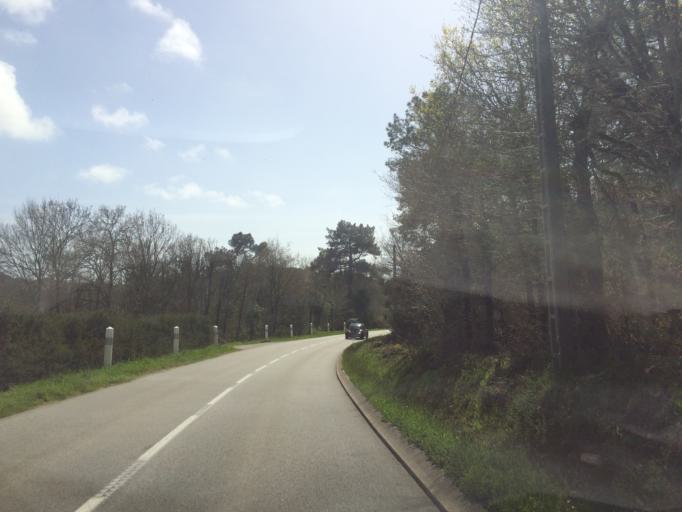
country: FR
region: Brittany
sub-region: Departement du Morbihan
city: Ploemel
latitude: 47.6333
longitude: -3.0475
